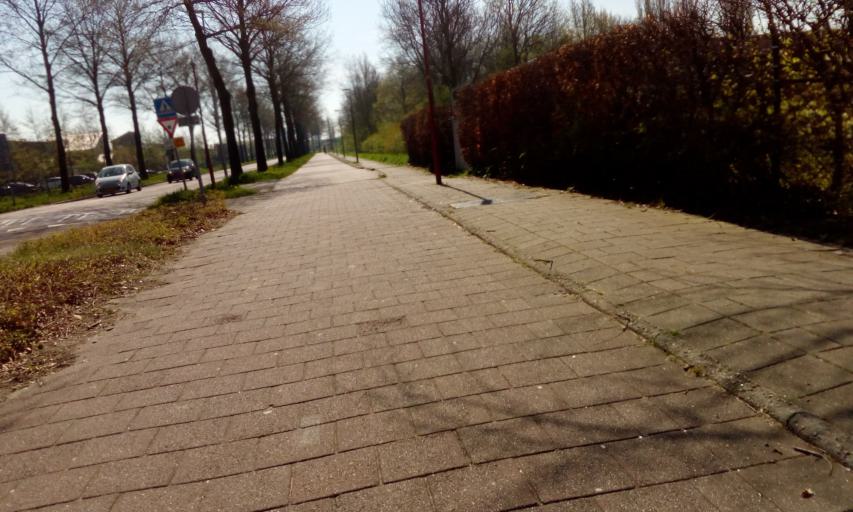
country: NL
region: South Holland
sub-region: Gemeente Rijnwoude
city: Benthuizen
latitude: 52.0707
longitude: 4.5196
